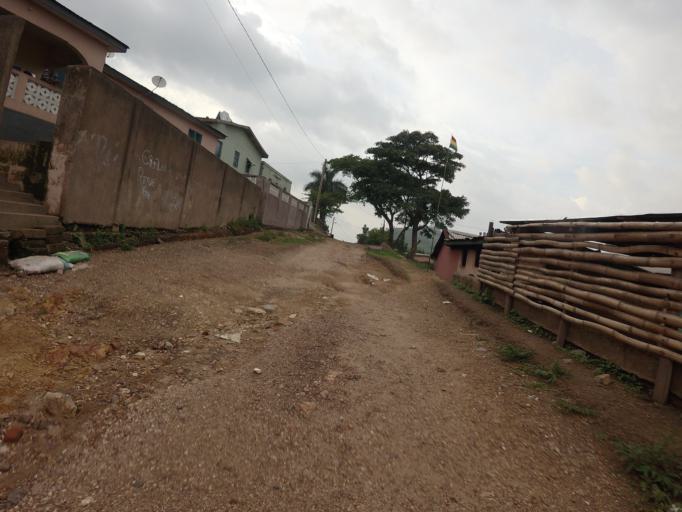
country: GH
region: Volta
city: Kpandu
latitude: 6.8484
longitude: 0.4353
